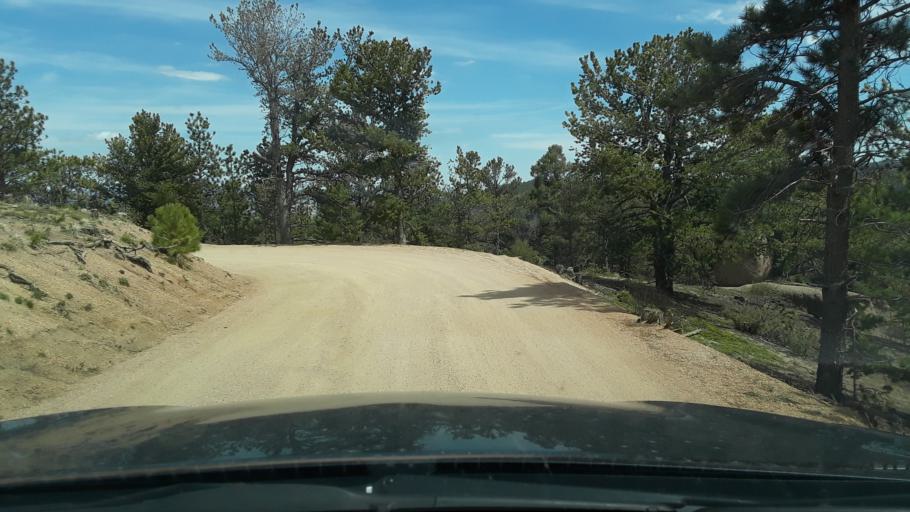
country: US
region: Colorado
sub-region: El Paso County
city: Palmer Lake
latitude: 39.0684
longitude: -104.9493
